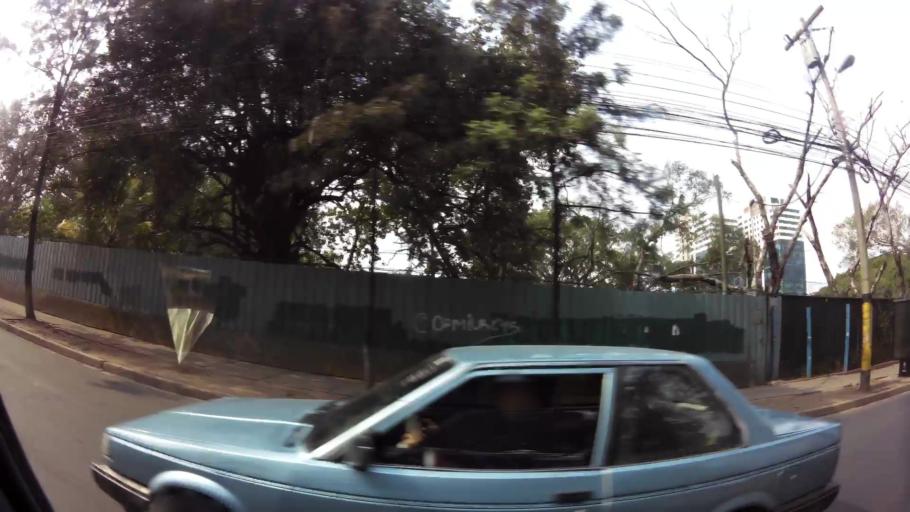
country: HN
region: Francisco Morazan
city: Tegucigalpa
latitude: 14.1028
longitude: -87.1813
